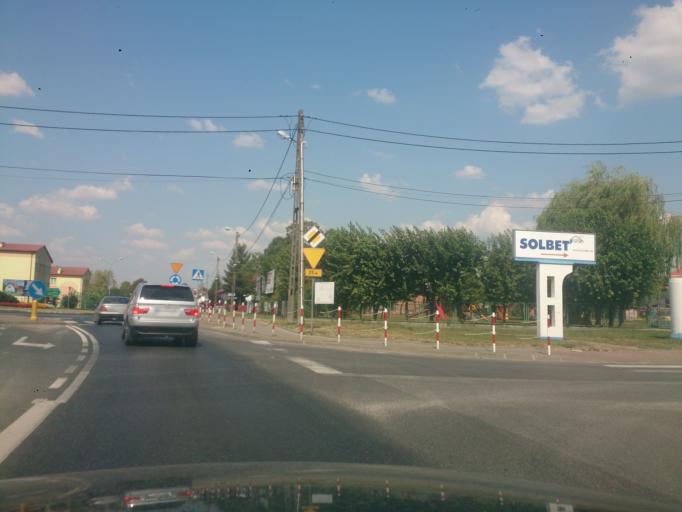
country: PL
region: Subcarpathian Voivodeship
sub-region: Powiat kolbuszowski
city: Kolbuszowa
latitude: 50.2435
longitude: 21.7791
